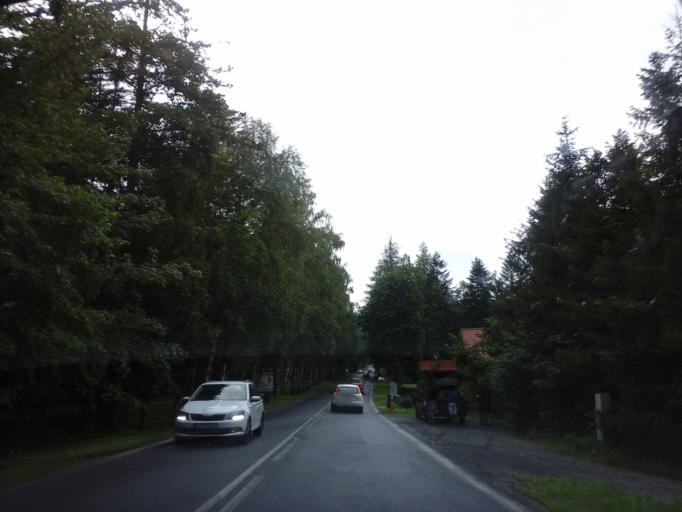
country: SK
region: Presovsky
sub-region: Okres Poprad
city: Zdiar
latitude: 49.2253
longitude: 20.3237
